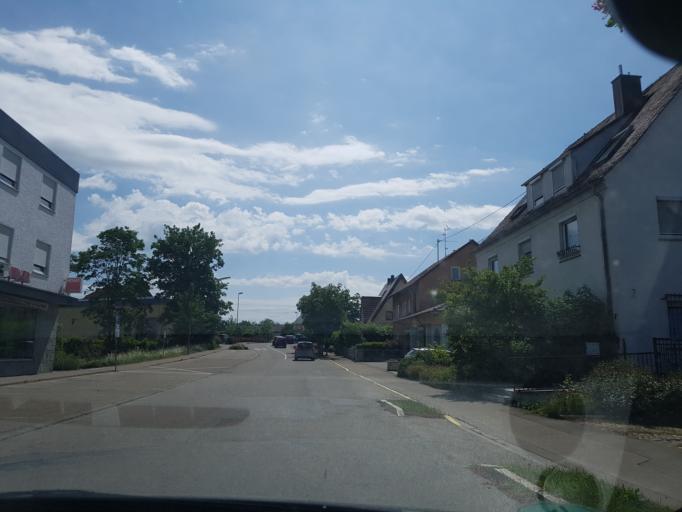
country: DE
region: Bavaria
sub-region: Swabia
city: Nersingen
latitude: 48.4293
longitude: 10.1198
